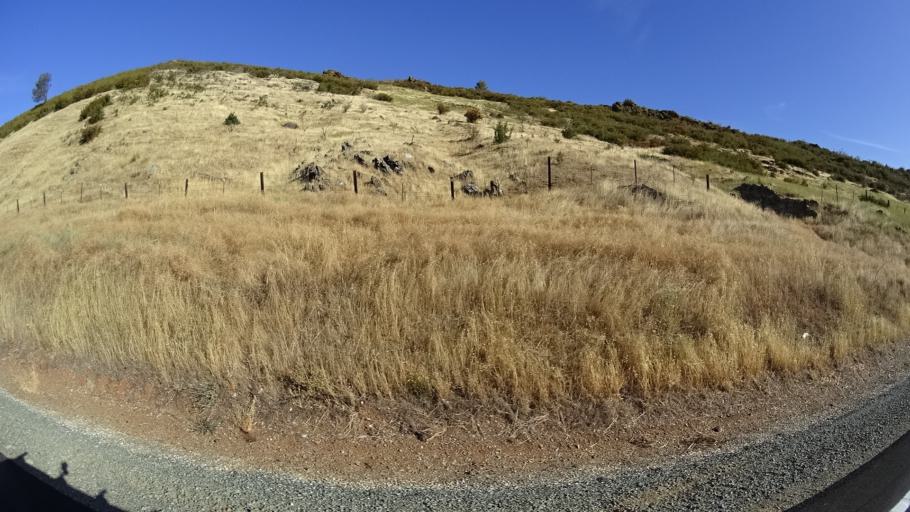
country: US
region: California
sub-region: Calaveras County
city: Valley Springs
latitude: 38.1994
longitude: -120.7980
